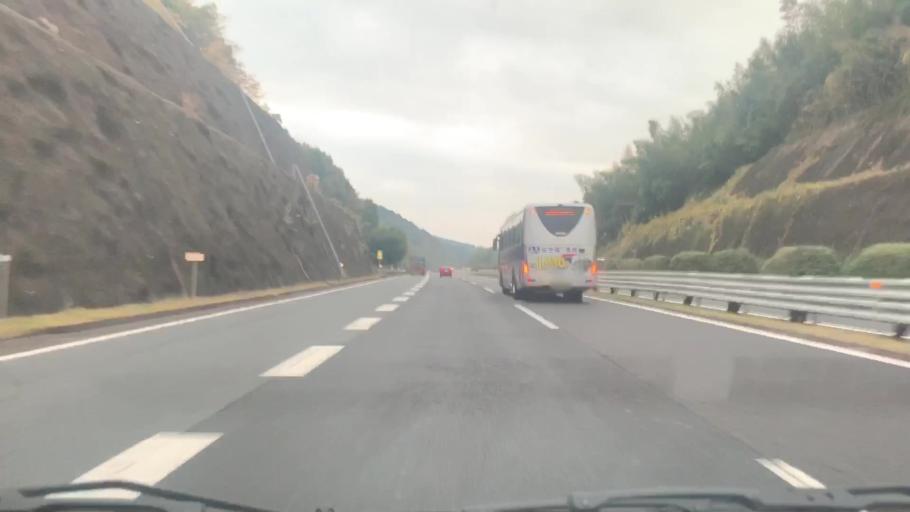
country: JP
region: Nagasaki
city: Omura
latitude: 32.9931
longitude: 129.9536
